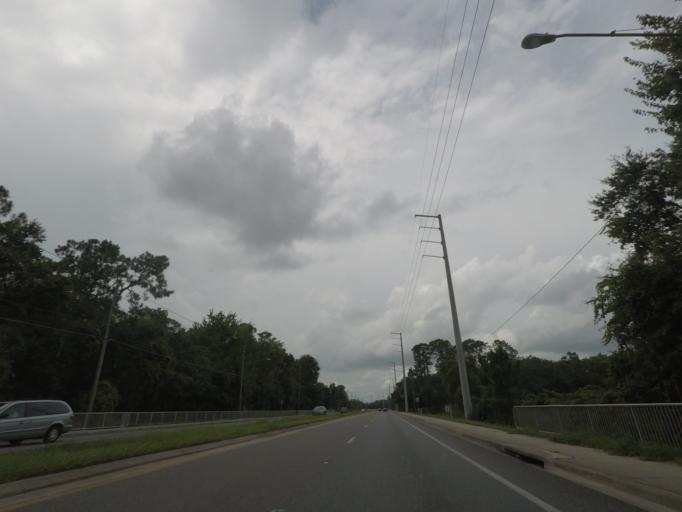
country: US
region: Florida
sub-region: Polk County
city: Loughman
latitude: 28.2440
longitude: -81.5745
